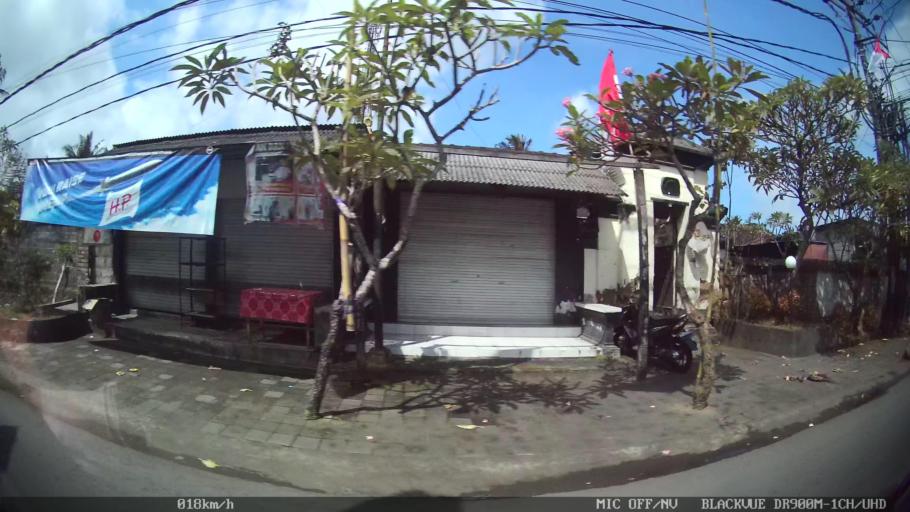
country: ID
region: Bali
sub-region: Kabupaten Gianyar
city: Ubud
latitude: -8.5297
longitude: 115.3001
